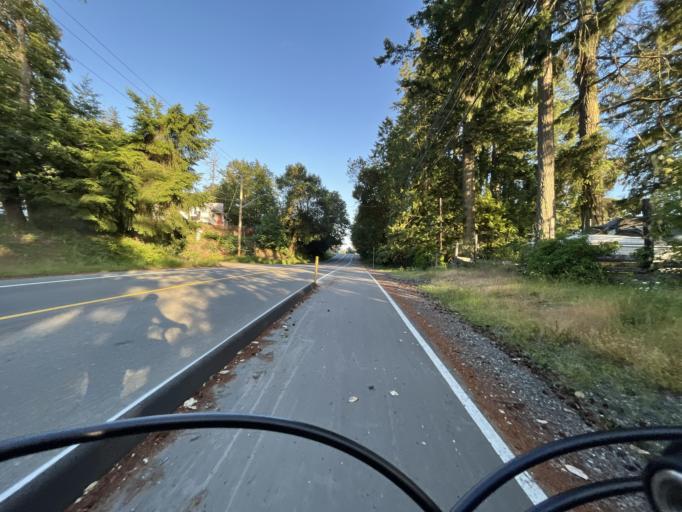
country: CA
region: British Columbia
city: Langford
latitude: 48.4525
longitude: -123.5291
